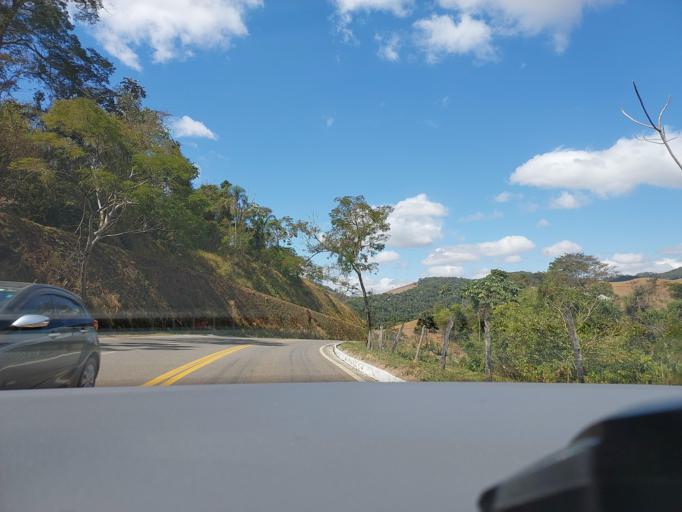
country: BR
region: Minas Gerais
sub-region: Mirai
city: Mirai
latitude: -21.0468
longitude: -42.5242
